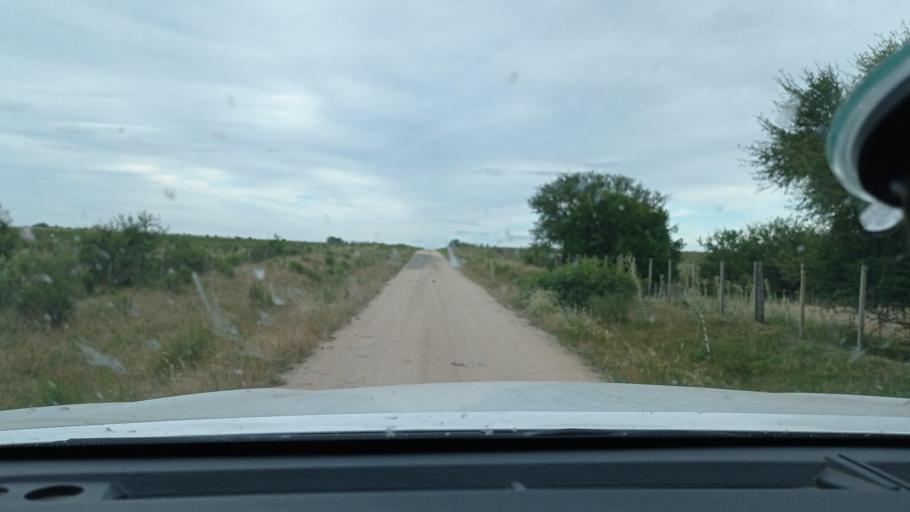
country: UY
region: Florida
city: Casupa
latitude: -34.1459
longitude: -55.7913
